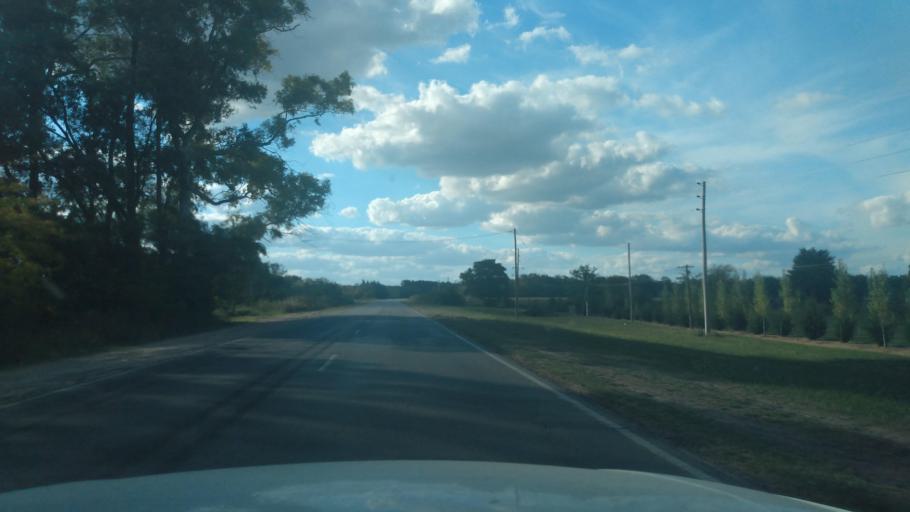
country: AR
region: Buenos Aires
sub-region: Partido de Mercedes
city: Mercedes
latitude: -34.6905
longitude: -59.4045
